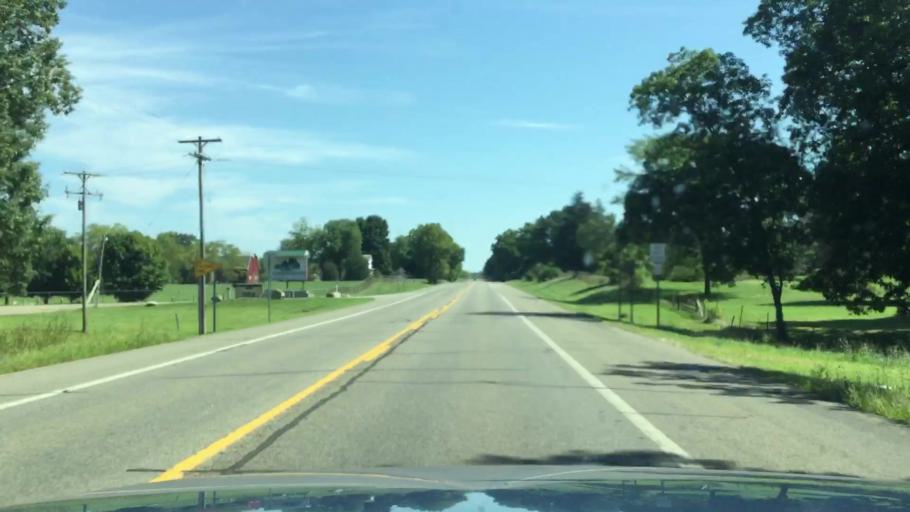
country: US
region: Michigan
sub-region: Jackson County
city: Brooklyn
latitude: 42.0560
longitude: -84.2573
